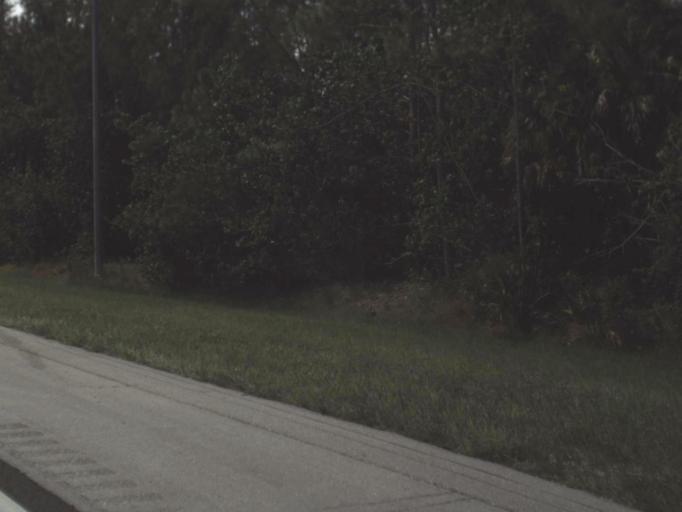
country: US
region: Florida
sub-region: Collier County
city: Vineyards
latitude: 26.2205
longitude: -81.7365
